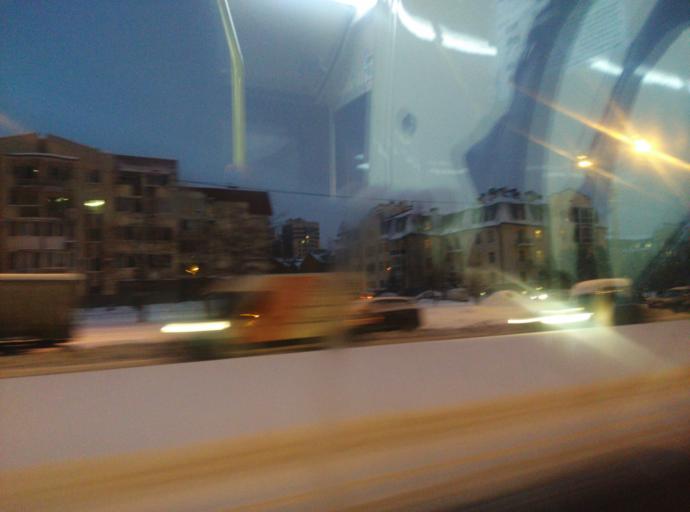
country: RU
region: St.-Petersburg
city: Kolomyagi
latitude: 60.0178
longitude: 30.2748
